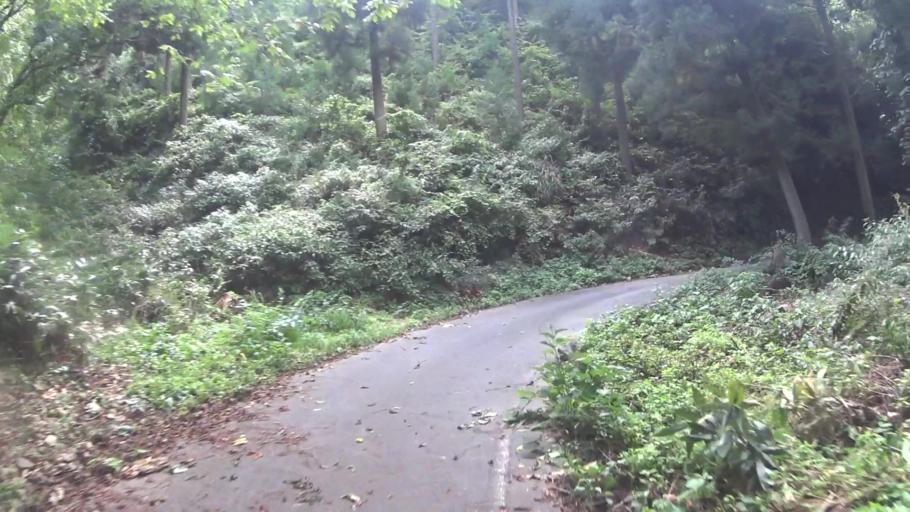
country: JP
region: Kyoto
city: Miyazu
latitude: 35.7351
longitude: 135.1956
